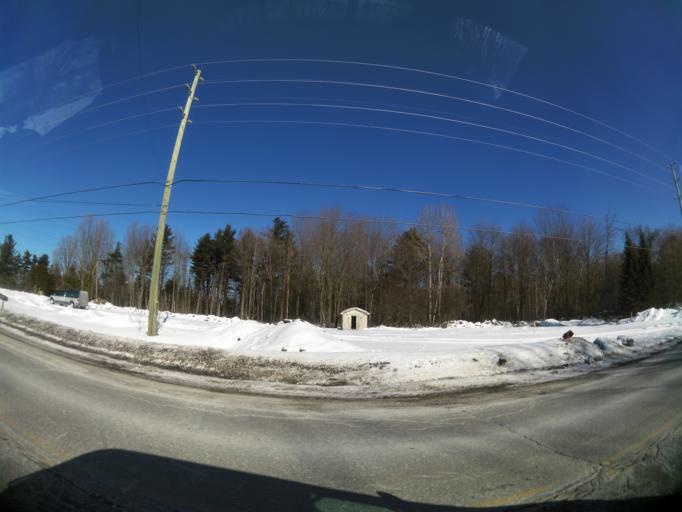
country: CA
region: Ontario
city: Ottawa
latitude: 45.4317
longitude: -75.5235
